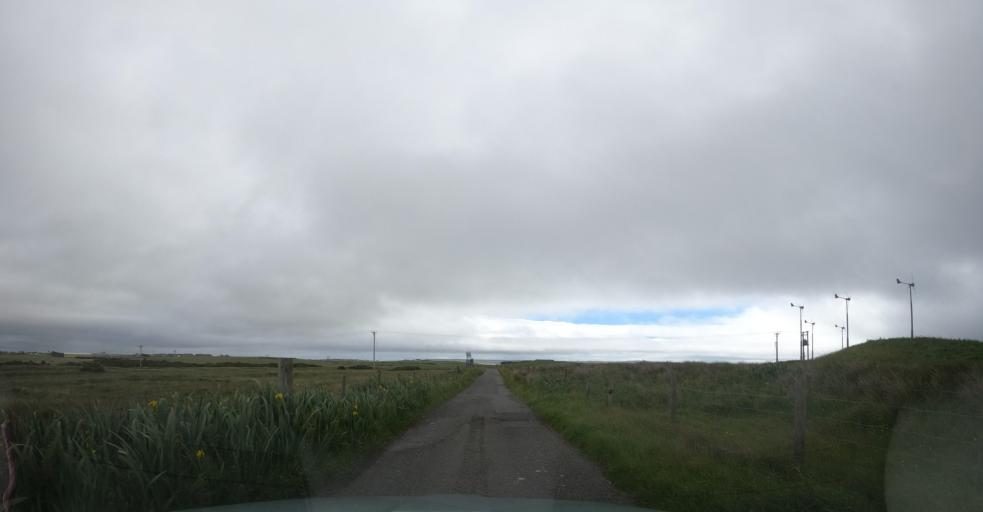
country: GB
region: Scotland
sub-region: Eilean Siar
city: Stornoway
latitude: 58.1922
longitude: -6.3502
